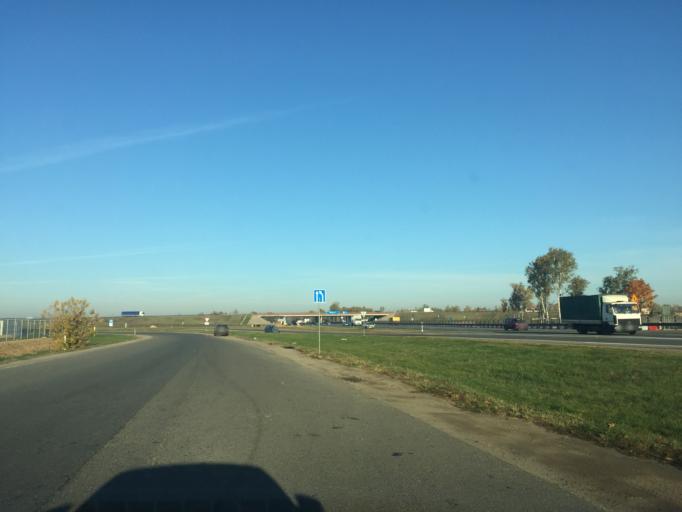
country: BY
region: Minsk
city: Pryvol'ny
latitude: 53.8021
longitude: 27.7983
